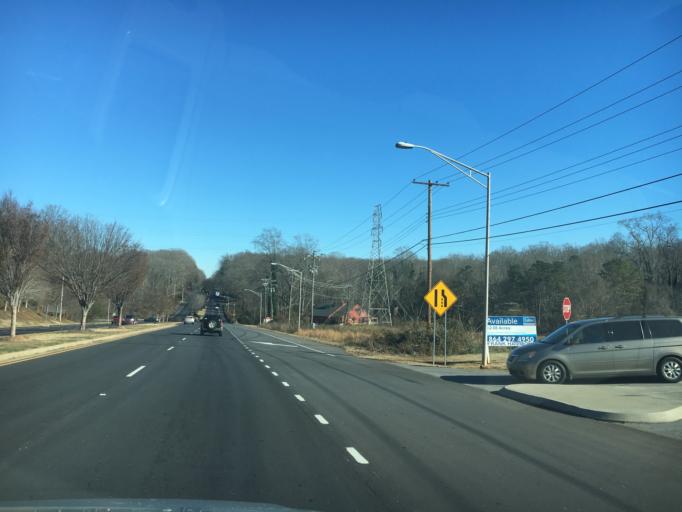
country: US
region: South Carolina
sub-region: Spartanburg County
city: Saxon
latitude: 34.9379
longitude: -81.9748
